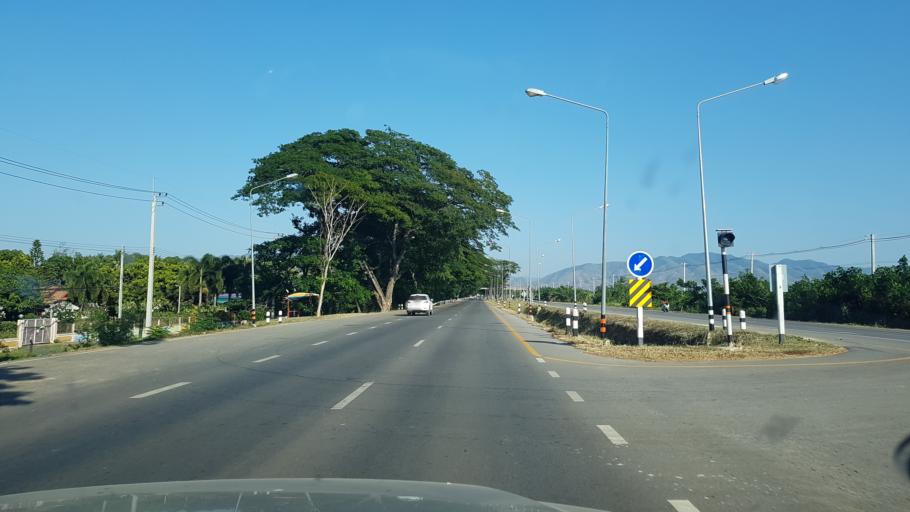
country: TH
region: Phetchabun
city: Lom Sak
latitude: 16.7271
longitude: 101.2579
